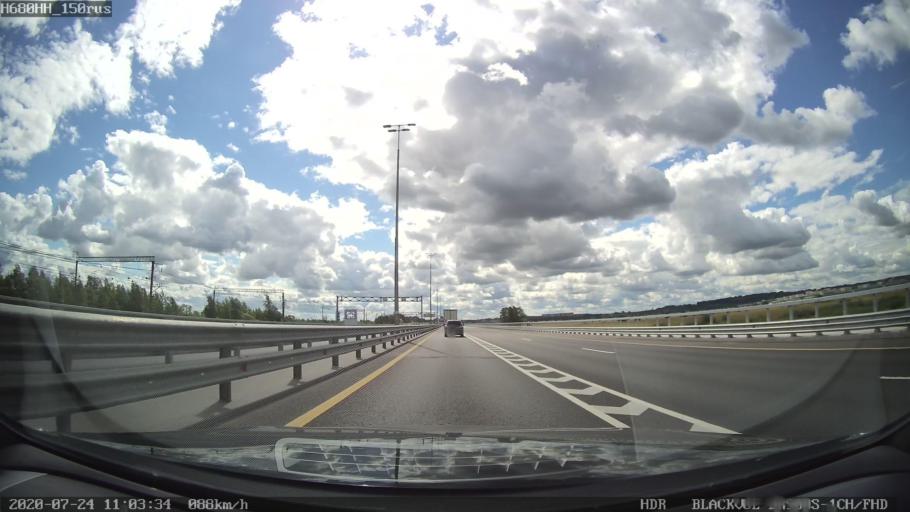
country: RU
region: St.-Petersburg
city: Shushary
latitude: 59.8009
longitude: 30.3388
